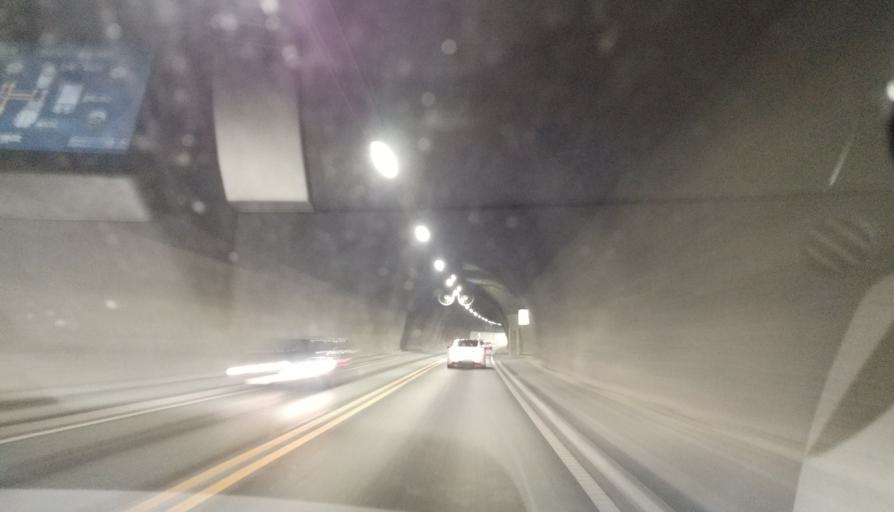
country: NO
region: Sor-Trondelag
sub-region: Malvik
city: Hommelvik
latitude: 63.4089
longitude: 10.7788
